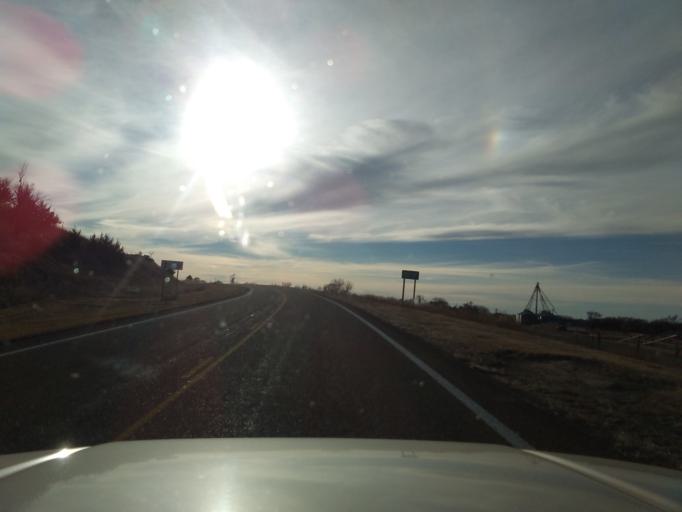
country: US
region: Kansas
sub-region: Norton County
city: Norton
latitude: 39.7404
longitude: -100.1708
